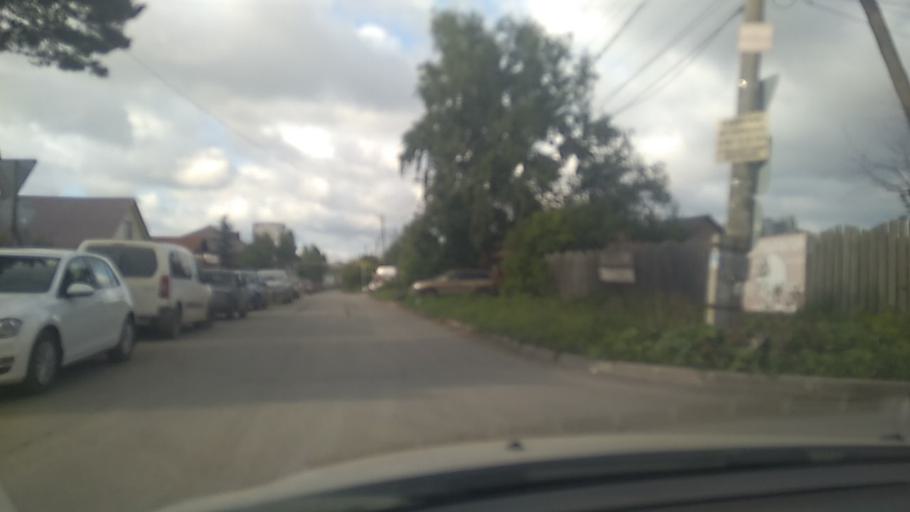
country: RU
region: Sverdlovsk
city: Shirokaya Rechka
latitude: 56.8045
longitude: 60.5036
